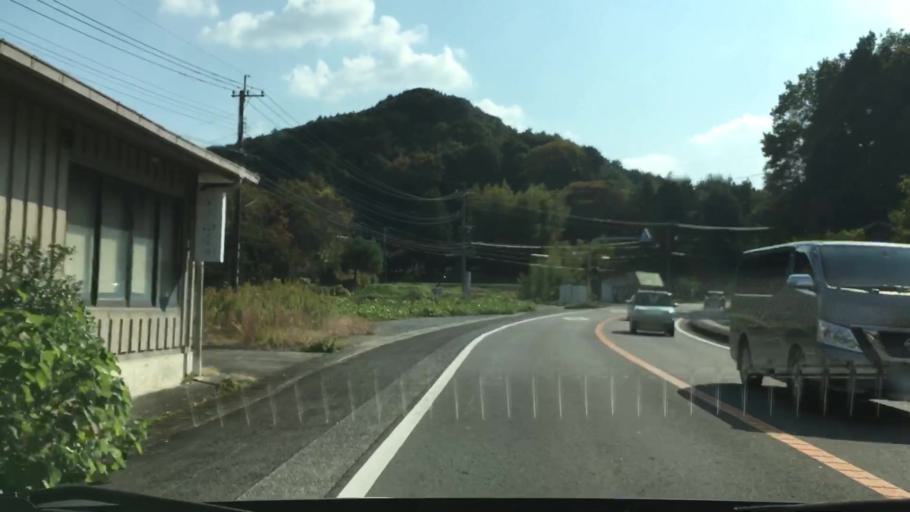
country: JP
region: Nagasaki
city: Togitsu
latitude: 32.9762
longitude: 129.7817
